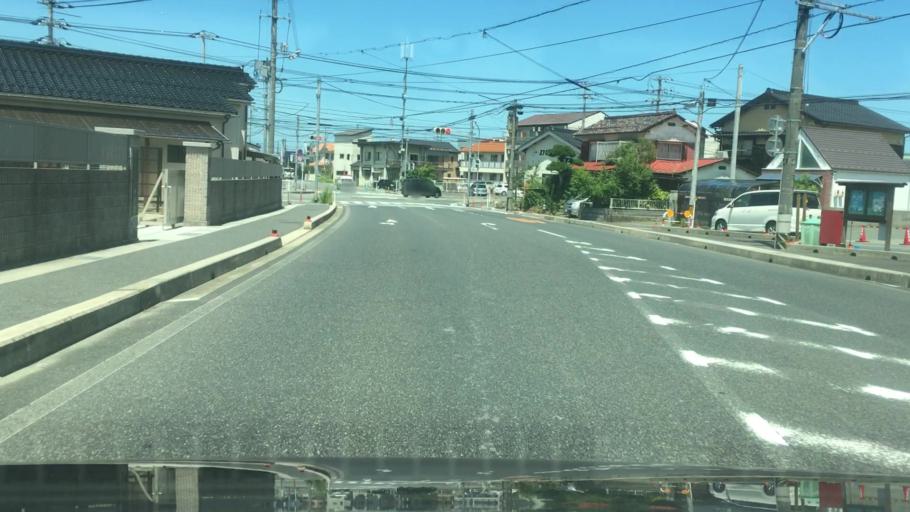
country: JP
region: Tottori
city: Tottori
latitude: 35.4840
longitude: 134.2277
